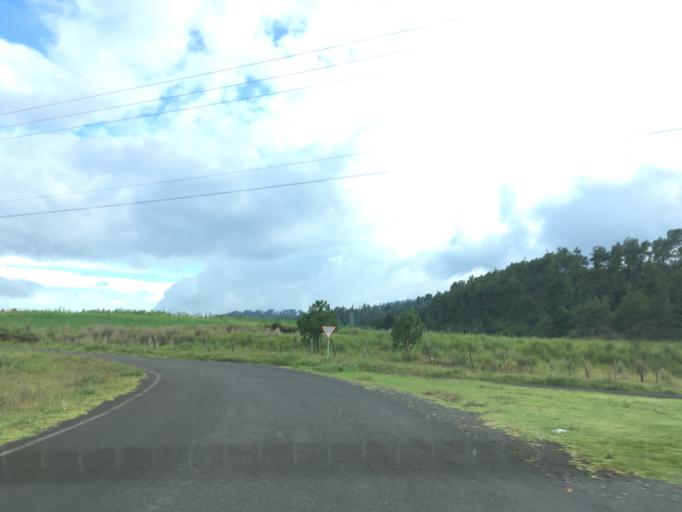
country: MX
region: Michoacan
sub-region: Nahuatzen
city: Sevina
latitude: 19.6125
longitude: -101.8592
